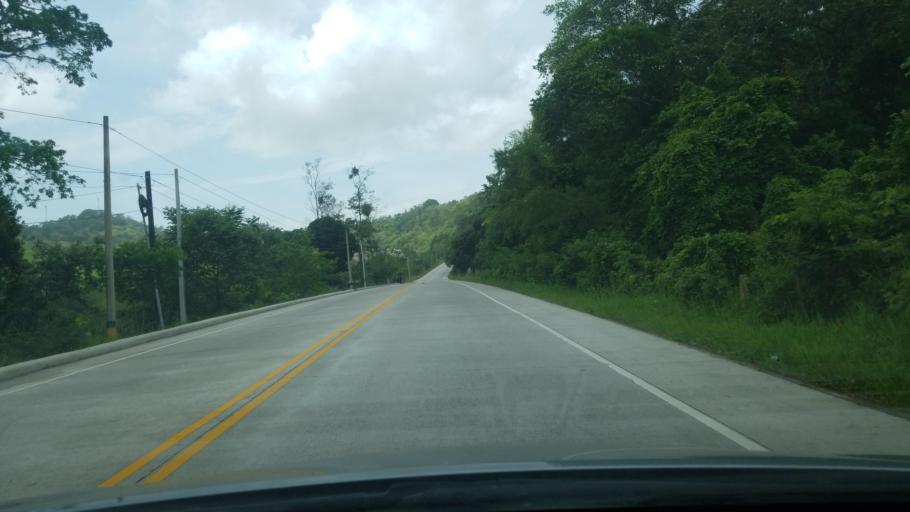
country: HN
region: Copan
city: Veracruz
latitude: 14.9249
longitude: -88.7647
